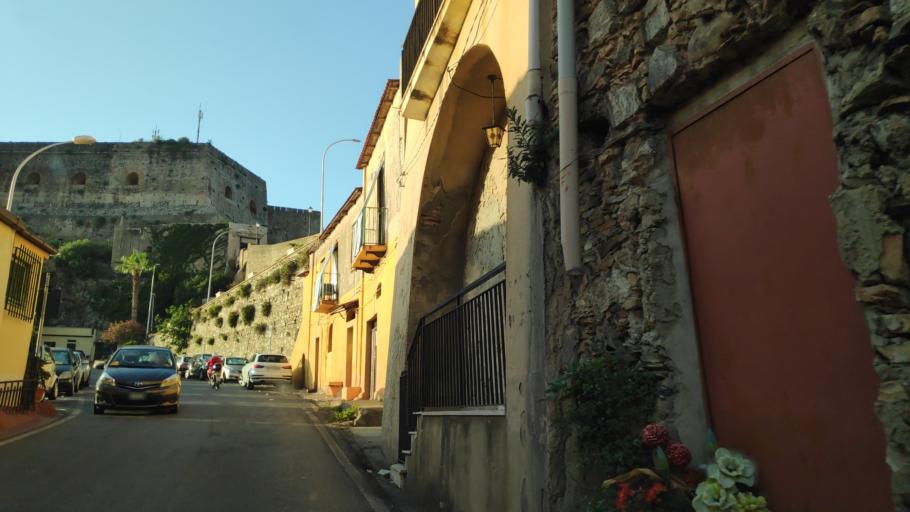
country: IT
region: Calabria
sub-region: Provincia di Reggio Calabria
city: Scilla
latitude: 38.2548
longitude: 15.7151
